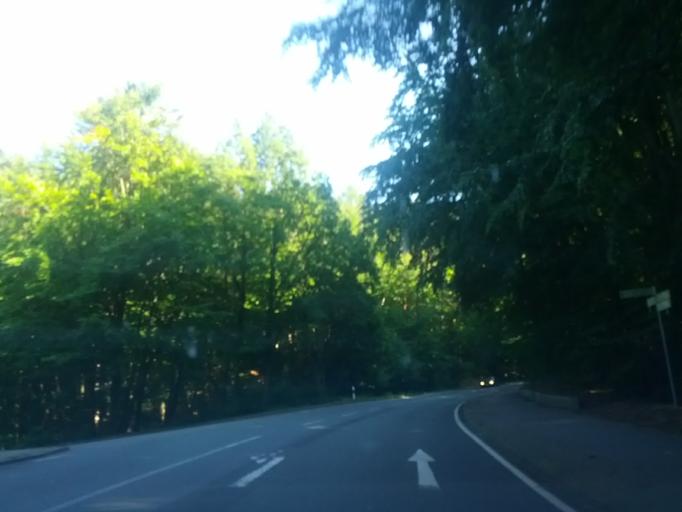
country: DE
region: Mecklenburg-Vorpommern
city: Ostseebad Gohren
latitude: 54.3433
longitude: 13.7201
